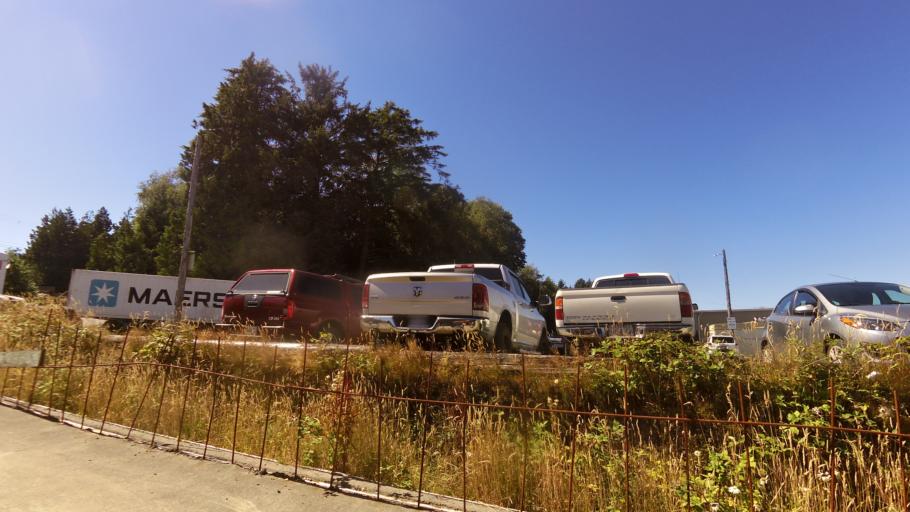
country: CA
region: British Columbia
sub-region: Regional District of Alberni-Clayoquot
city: Ucluelet
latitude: 48.9438
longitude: -125.5465
